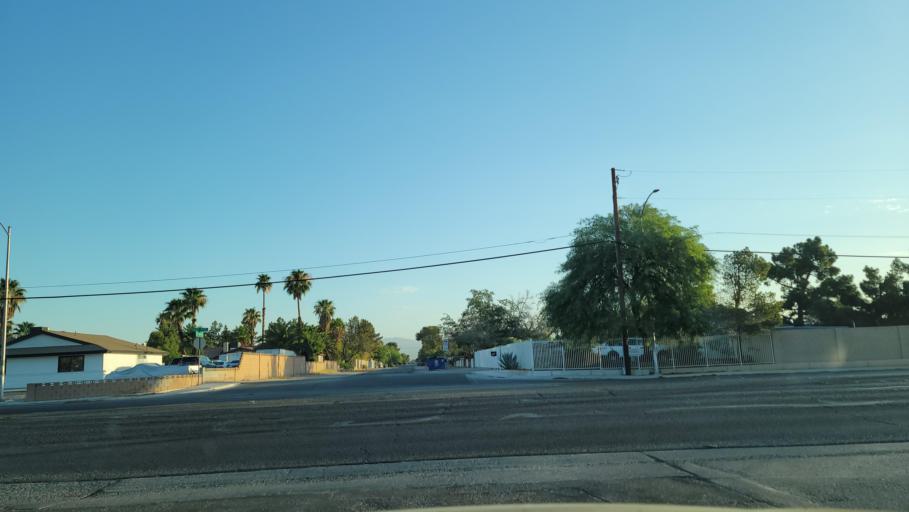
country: US
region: Nevada
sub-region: Clark County
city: Spring Valley
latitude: 36.1290
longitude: -115.2294
